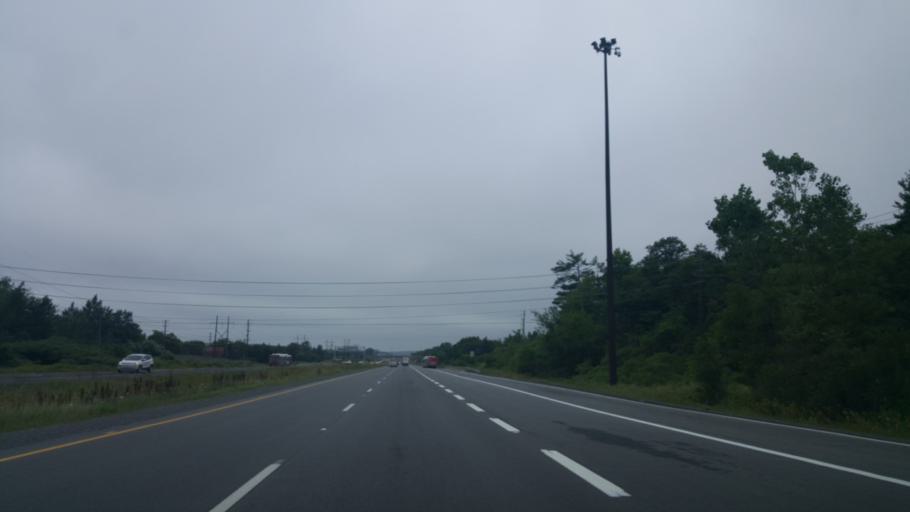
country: CA
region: Quebec
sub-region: Outaouais
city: Gatineau
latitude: 45.4773
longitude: -75.5251
